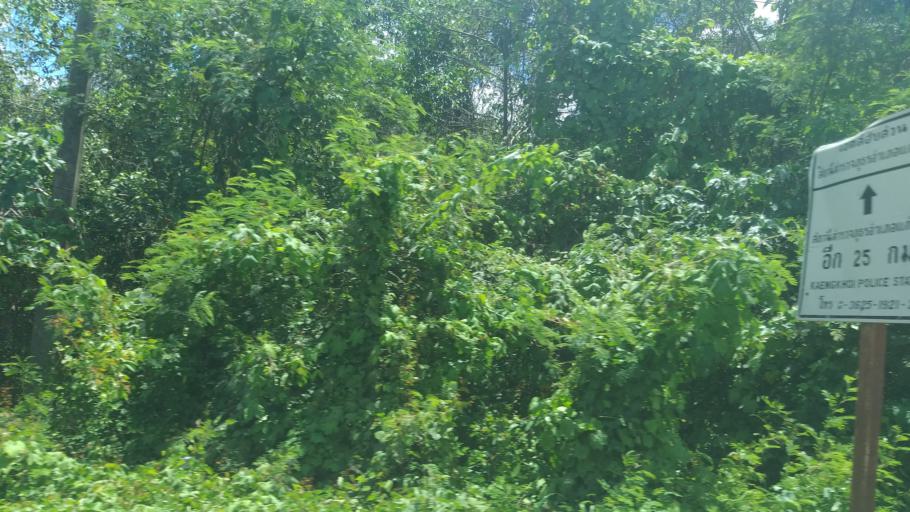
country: TH
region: Sara Buri
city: Wihan Daeng
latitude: 14.3845
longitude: 101.0937
